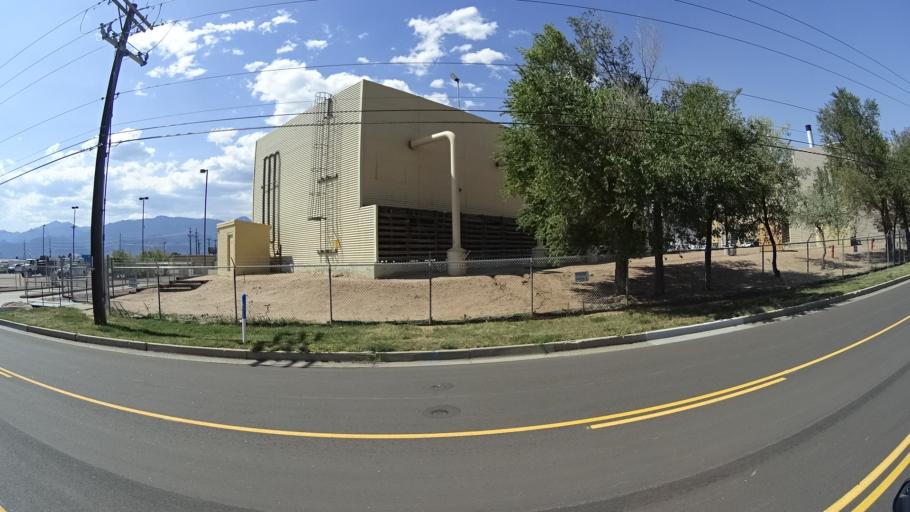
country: US
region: Colorado
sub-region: El Paso County
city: Colorado Springs
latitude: 38.8801
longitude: -104.8159
